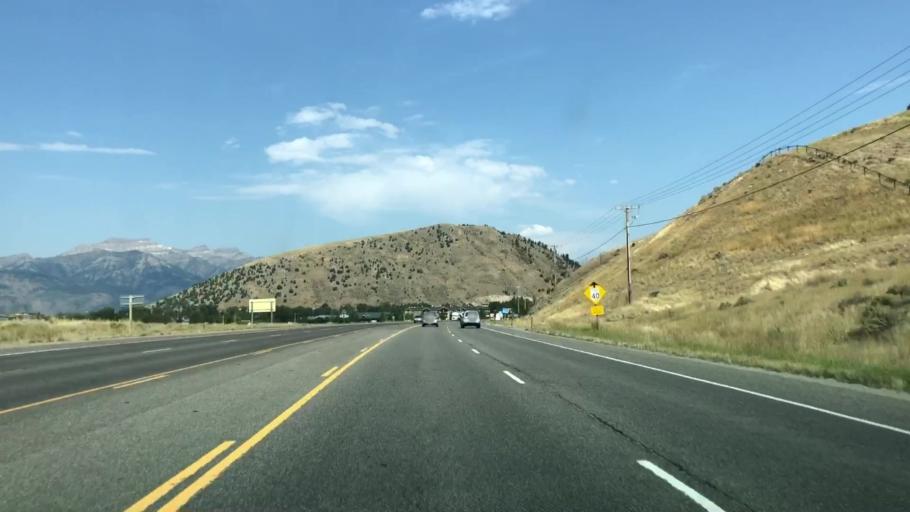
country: US
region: Wyoming
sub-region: Teton County
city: Rafter J Ranch
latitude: 43.4520
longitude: -110.7922
